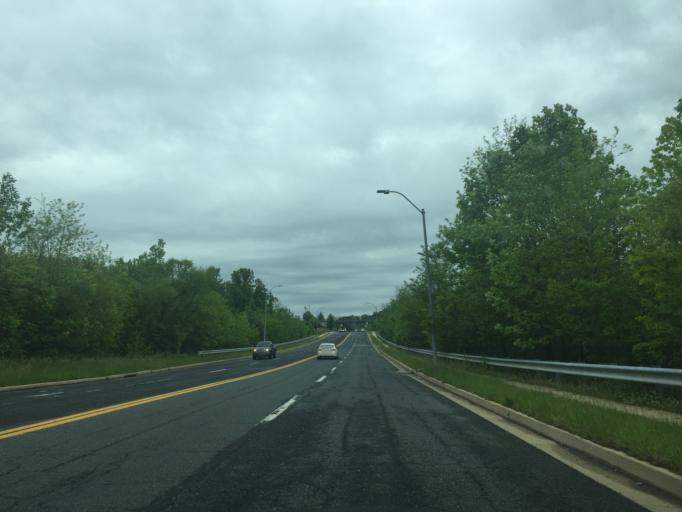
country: US
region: Maryland
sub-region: Baltimore County
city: Perry Hall
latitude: 39.3993
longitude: -76.4493
